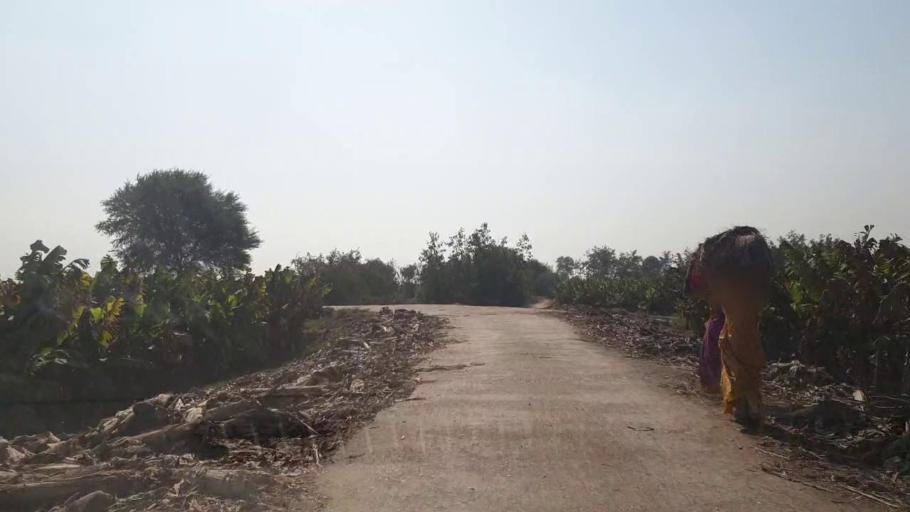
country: PK
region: Sindh
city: Tando Jam
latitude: 25.3414
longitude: 68.6019
